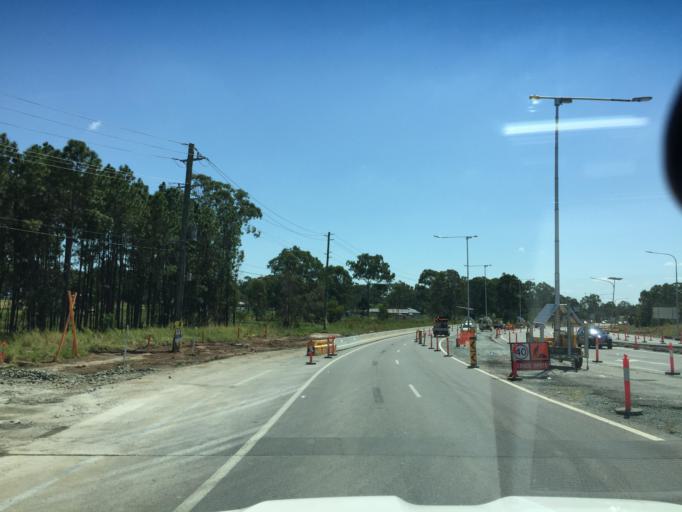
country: AU
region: Queensland
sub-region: Moreton Bay
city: Burpengary
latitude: -27.1790
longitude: 152.9811
